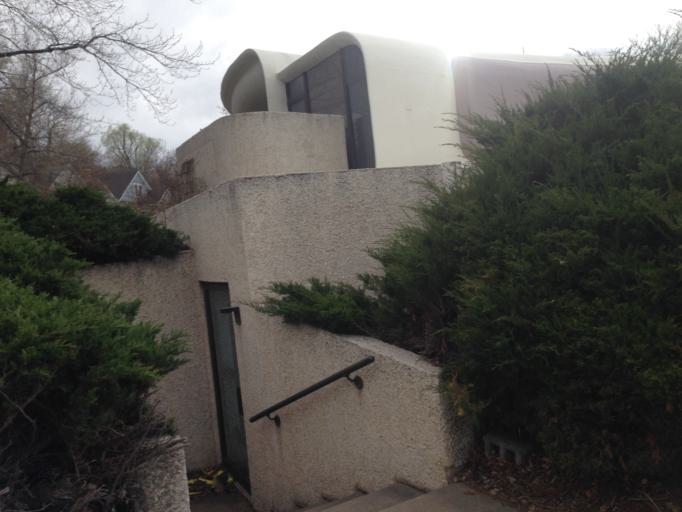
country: US
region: Colorado
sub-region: Boulder County
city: Boulder
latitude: 40.0220
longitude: -105.2816
